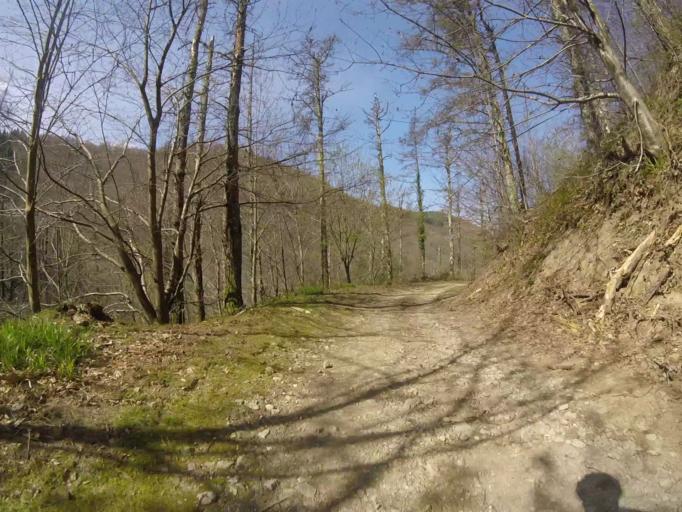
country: ES
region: Basque Country
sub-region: Provincia de Guipuzcoa
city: Irun
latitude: 43.2572
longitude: -1.8074
